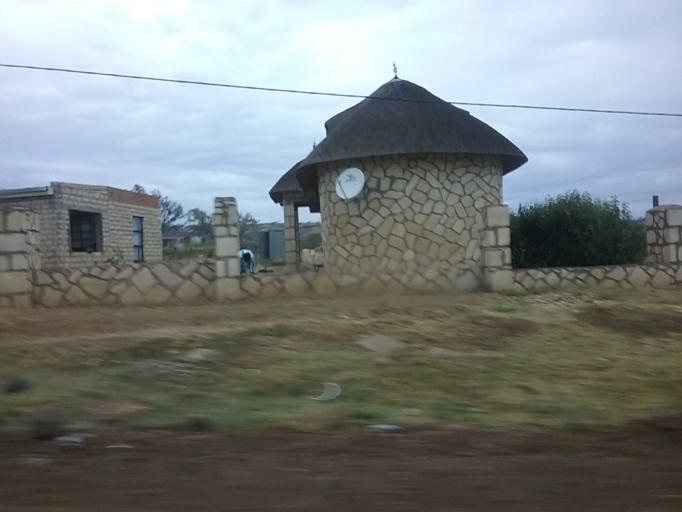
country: LS
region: Berea
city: Teyateyaneng
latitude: -29.1253
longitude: 27.7592
